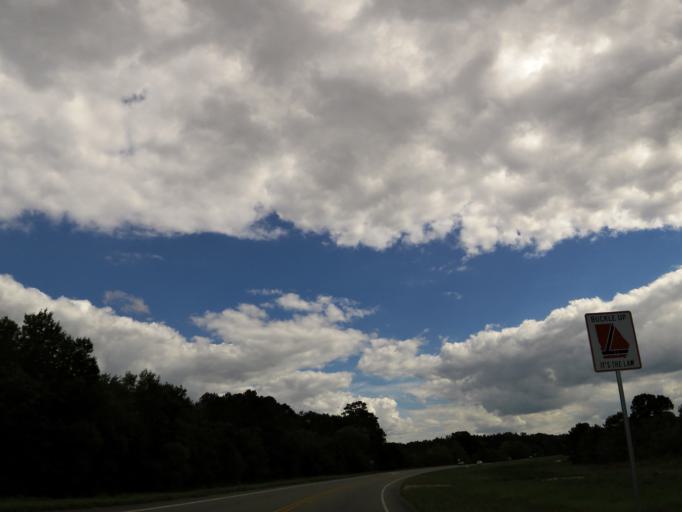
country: US
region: Tennessee
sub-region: Hamilton County
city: Lookout Mountain
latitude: 34.9782
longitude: -85.3332
